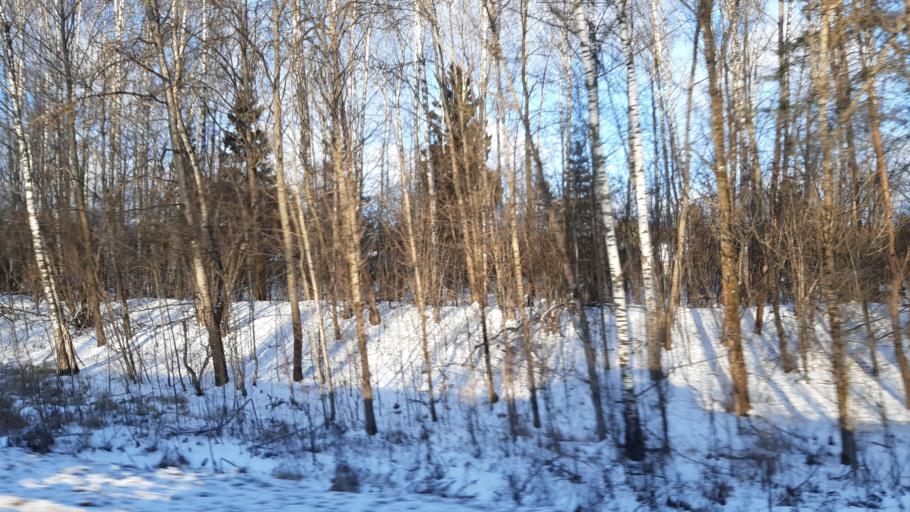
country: RU
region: Vladimir
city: Arsaki
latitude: 56.2977
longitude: 38.3596
